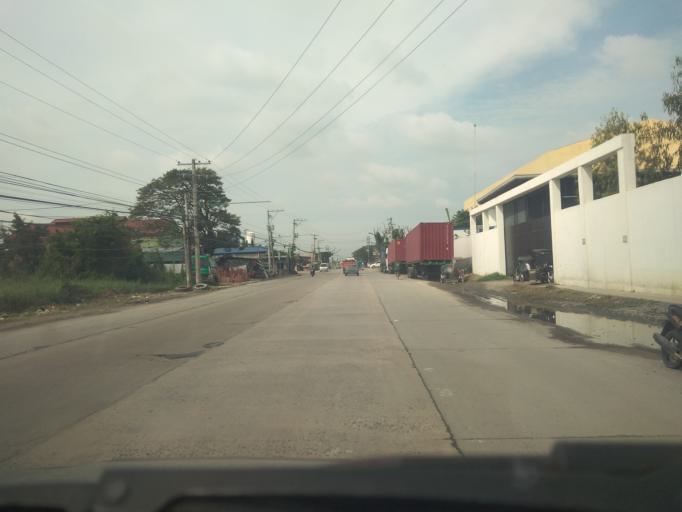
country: PH
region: Central Luzon
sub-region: Province of Pampanga
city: Santo Domingo
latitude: 15.0029
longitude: 120.7230
